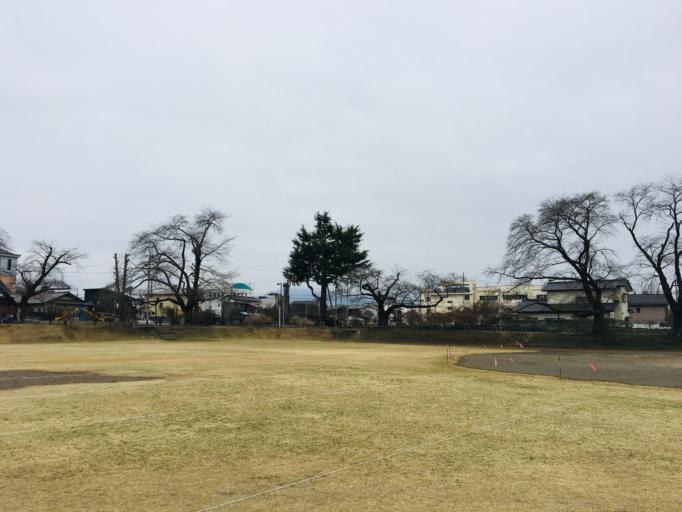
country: JP
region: Gunma
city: Numata
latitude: 36.6481
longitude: 139.0409
